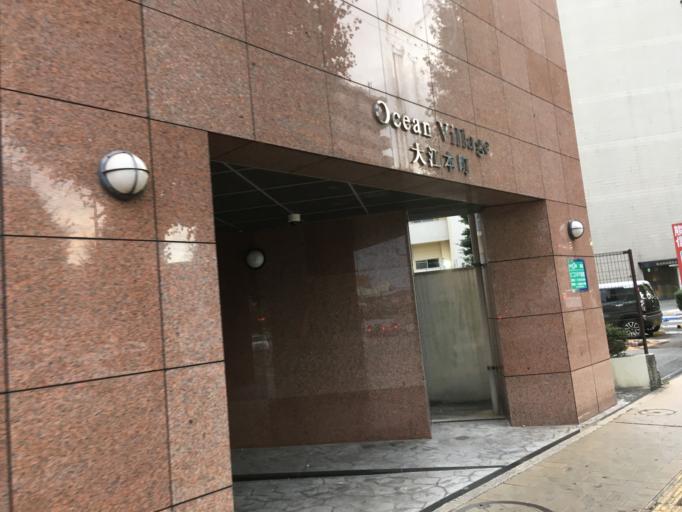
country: JP
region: Kumamoto
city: Kumamoto
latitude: 32.7966
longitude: 130.7212
